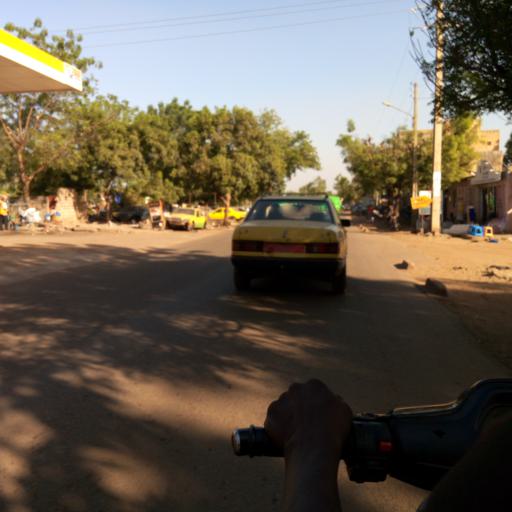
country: ML
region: Bamako
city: Bamako
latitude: 12.6559
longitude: -8.0255
